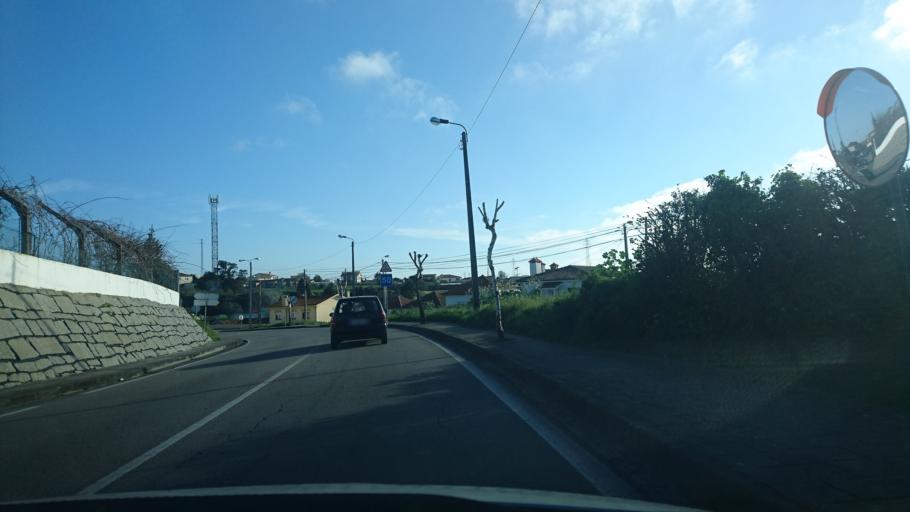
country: PT
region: Aveiro
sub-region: Espinho
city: Souto
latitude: 40.9780
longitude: -8.6319
